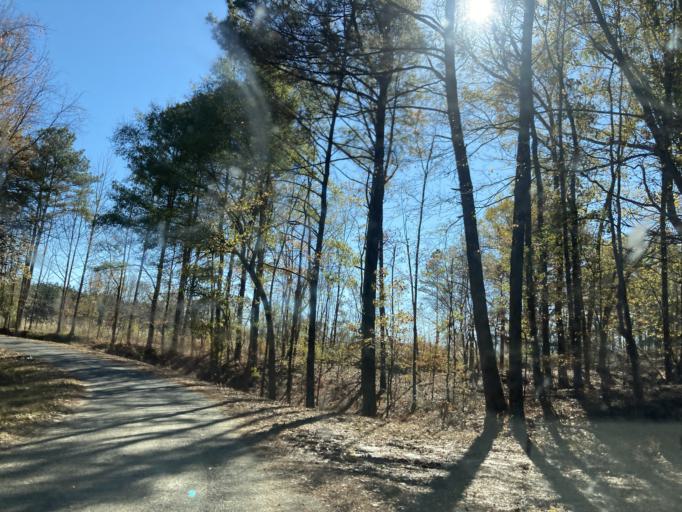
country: US
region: Mississippi
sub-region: Hinds County
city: Lynchburg
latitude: 32.5737
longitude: -90.5488
